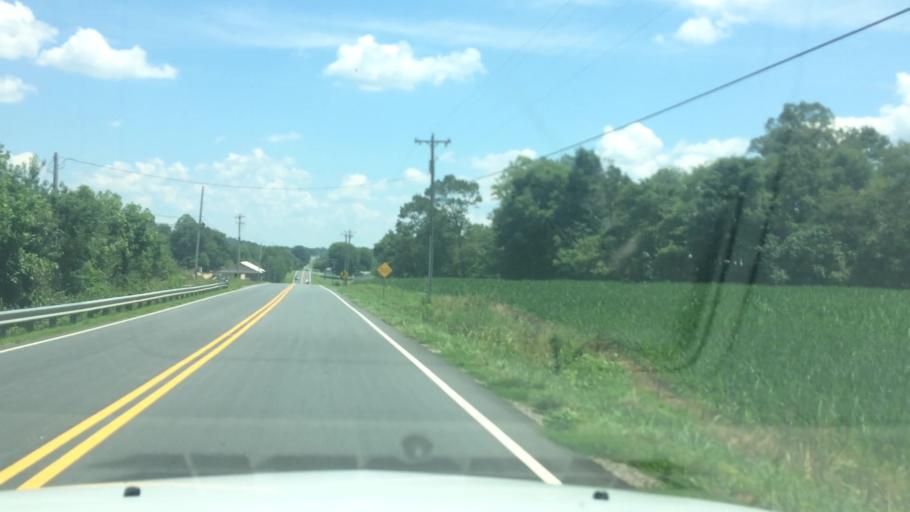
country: US
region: North Carolina
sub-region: Alexander County
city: Taylorsville
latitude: 35.9196
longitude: -81.2320
